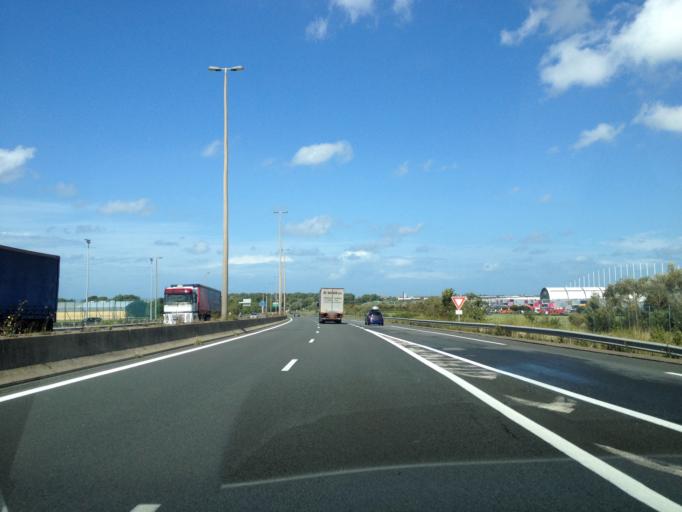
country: FR
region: Nord-Pas-de-Calais
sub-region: Departement du Pas-de-Calais
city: Coquelles
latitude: 50.9290
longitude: 1.8040
